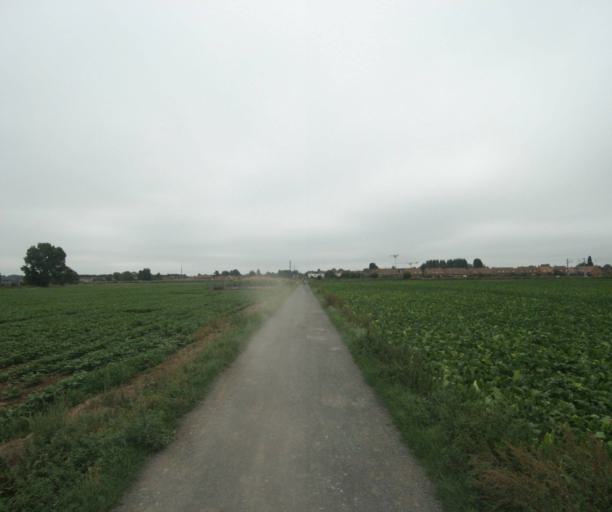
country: FR
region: Nord-Pas-de-Calais
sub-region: Departement du Nord
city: Willems
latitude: 50.6204
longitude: 3.2243
